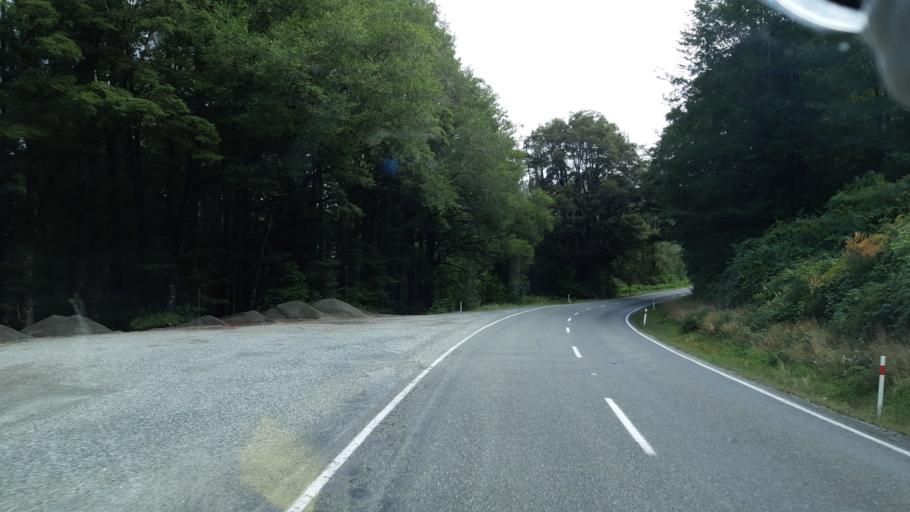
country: NZ
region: West Coast
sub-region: Buller District
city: Westport
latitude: -41.9800
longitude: 172.2043
